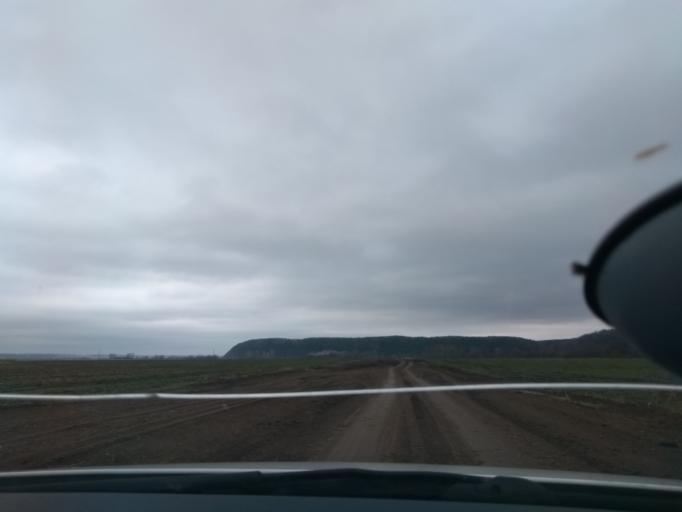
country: RU
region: Perm
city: Orda
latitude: 57.2505
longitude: 56.6202
